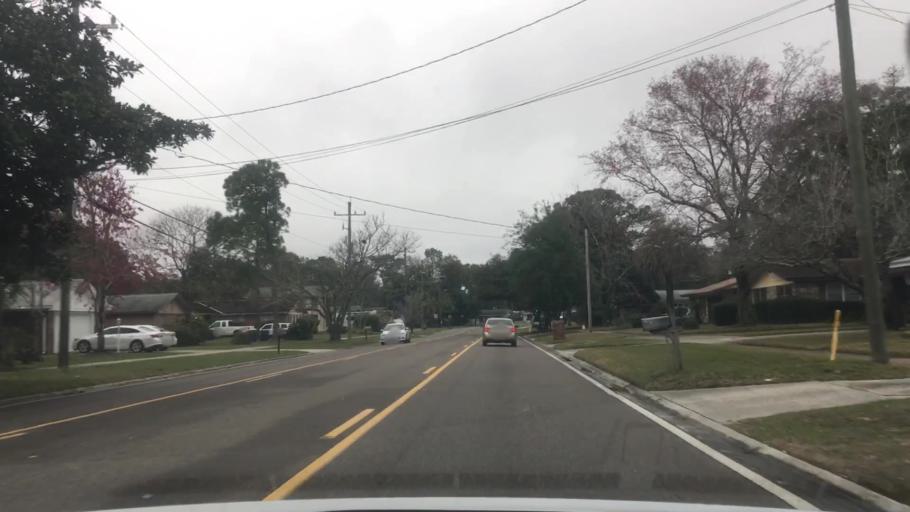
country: US
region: Florida
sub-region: Duval County
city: Jacksonville
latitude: 30.3547
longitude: -81.5781
